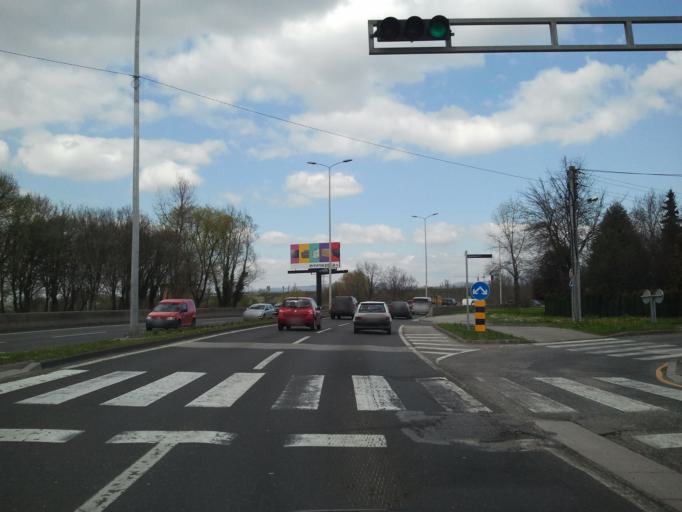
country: HR
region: Grad Zagreb
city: Odra
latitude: 45.7503
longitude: 15.9897
